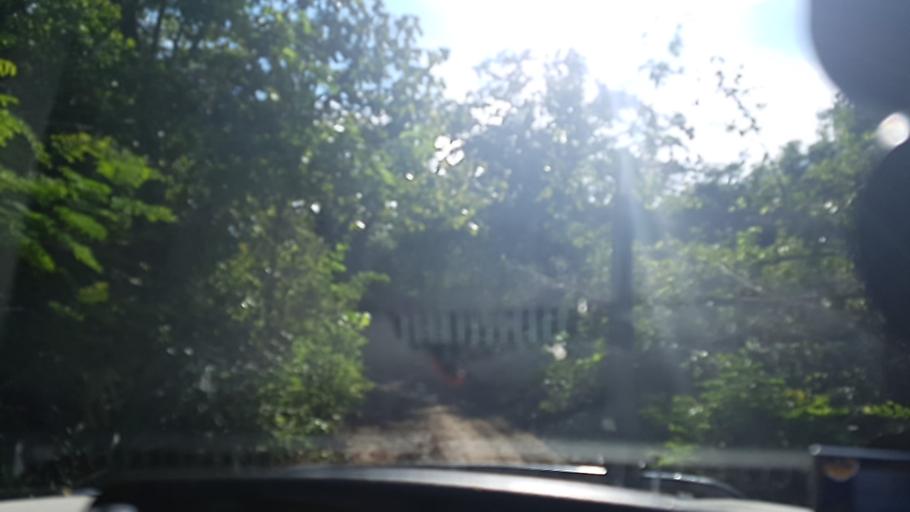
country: NI
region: Rivas
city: Tola
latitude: 11.5347
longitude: -86.1334
